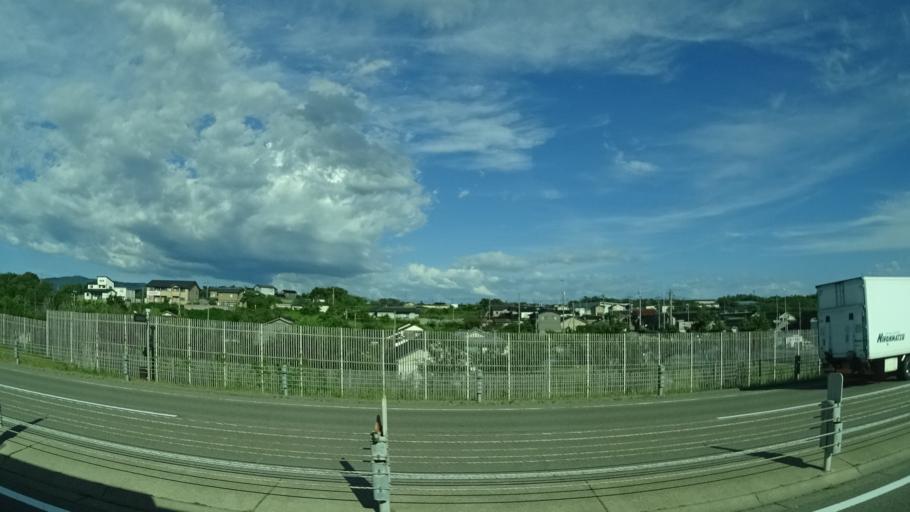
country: JP
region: Ishikawa
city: Tsubata
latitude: 36.7626
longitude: 136.7102
